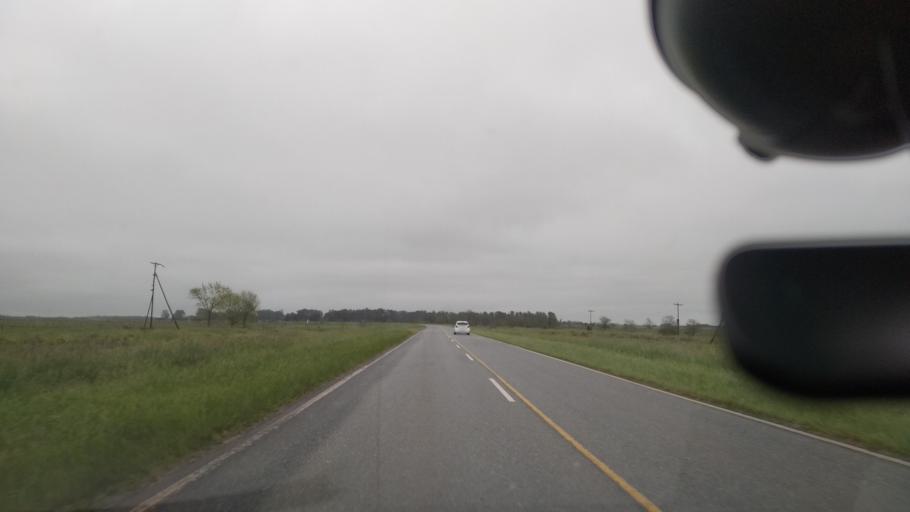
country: AR
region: Buenos Aires
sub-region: Partido de Magdalena
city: Magdalena
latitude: -35.2694
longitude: -57.6029
